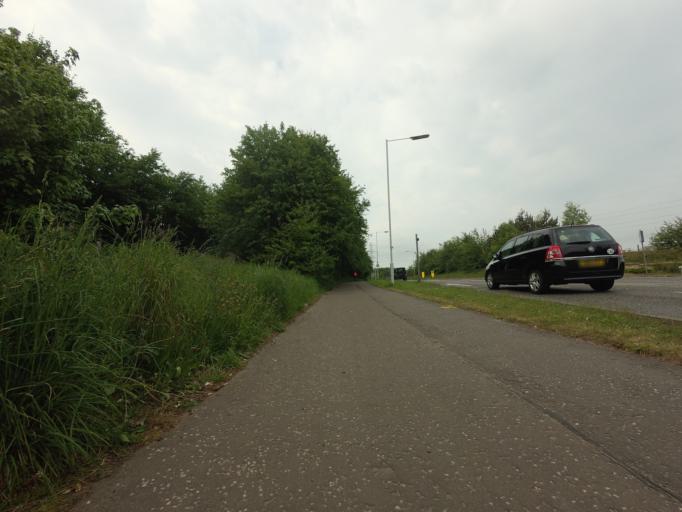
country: GB
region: Scotland
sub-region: Fife
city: Townhill
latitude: 56.0828
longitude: -3.4256
